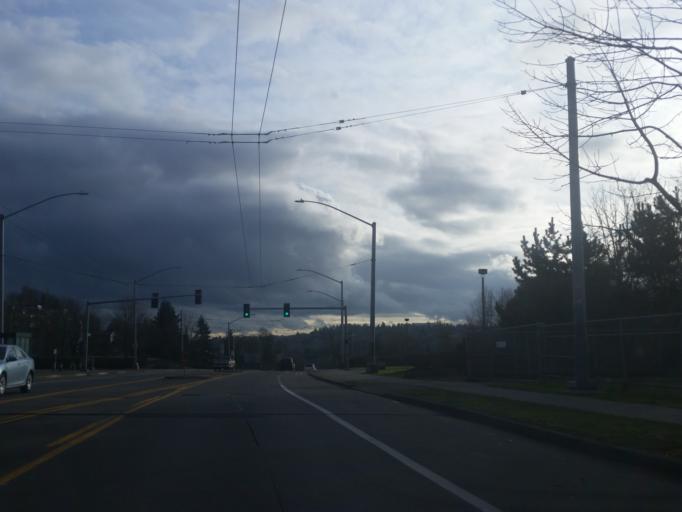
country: US
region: Washington
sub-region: King County
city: Seattle
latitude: 47.5909
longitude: -122.2976
